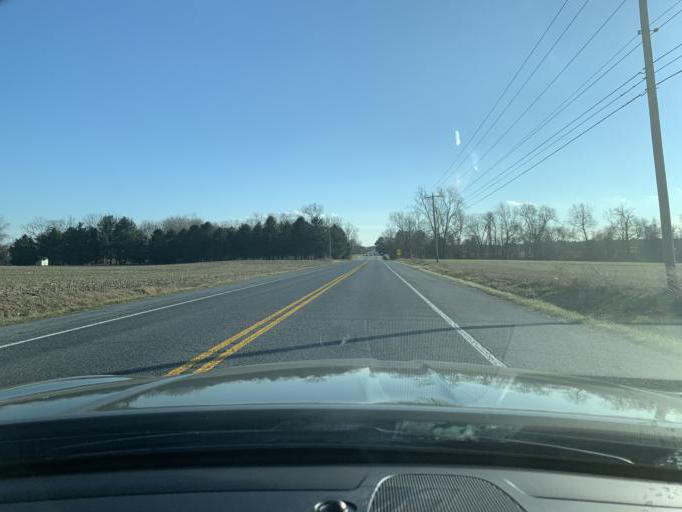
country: US
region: Maryland
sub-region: Queen Anne's County
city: Centreville
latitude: 39.0274
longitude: -76.0774
